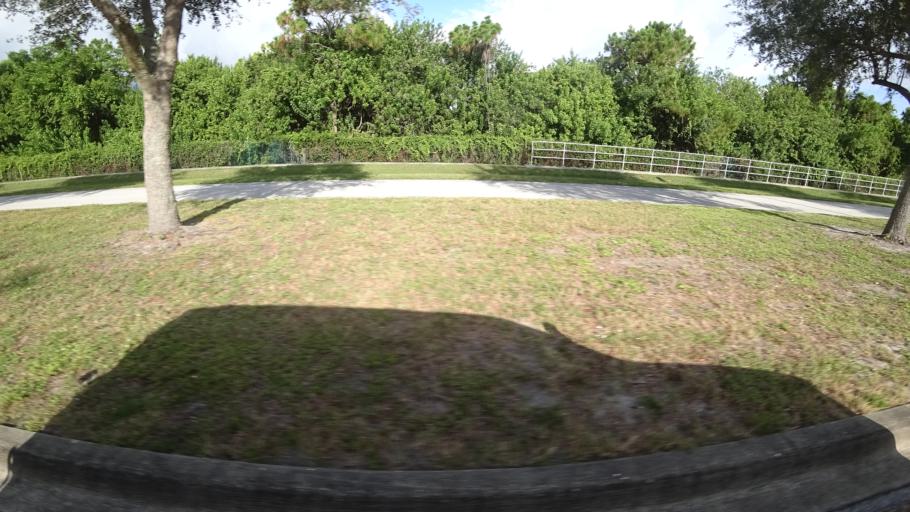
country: US
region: Florida
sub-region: Sarasota County
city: Desoto Lakes
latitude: 27.4015
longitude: -82.4631
